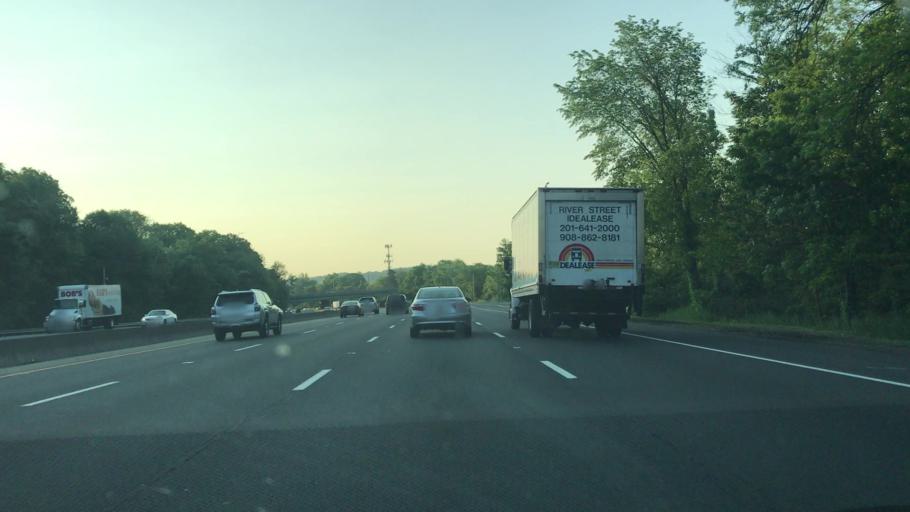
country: US
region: New Jersey
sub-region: Passaic County
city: Singac
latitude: 40.8978
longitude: -74.2275
